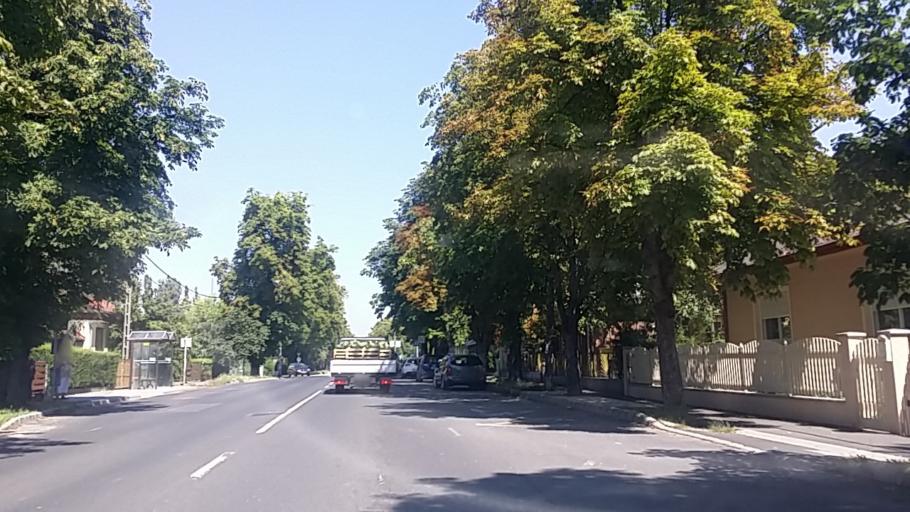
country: HU
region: Zala
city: Keszthely
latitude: 46.7641
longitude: 17.2375
